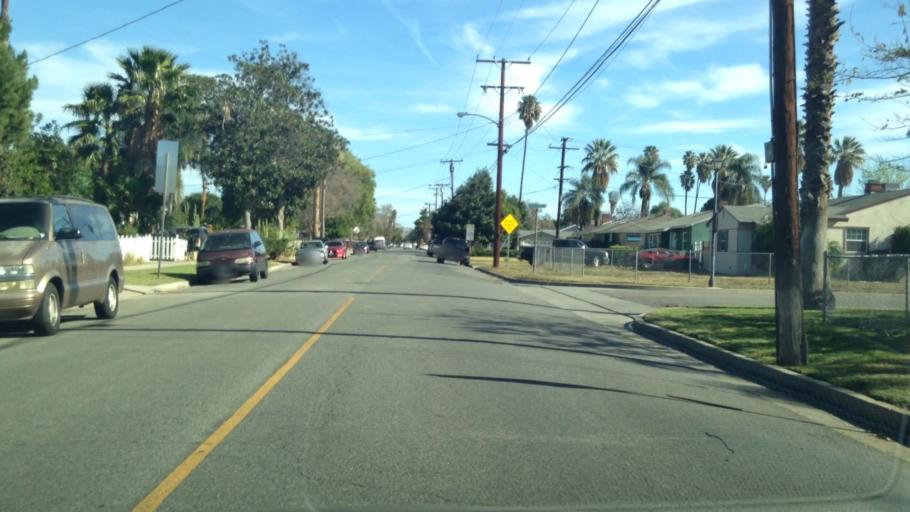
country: US
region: California
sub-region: Riverside County
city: Riverside
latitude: 33.9497
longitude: -117.4146
